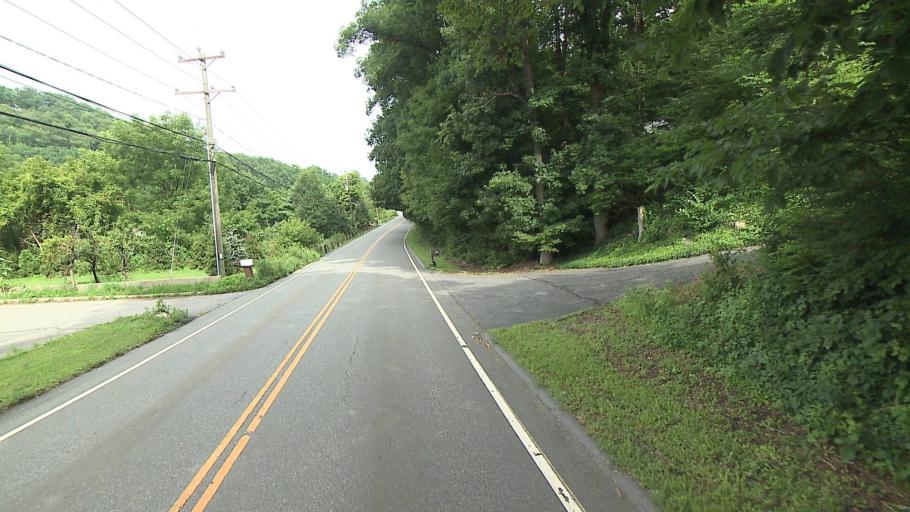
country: US
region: Connecticut
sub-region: Litchfield County
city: Kent
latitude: 41.7149
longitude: -73.4690
